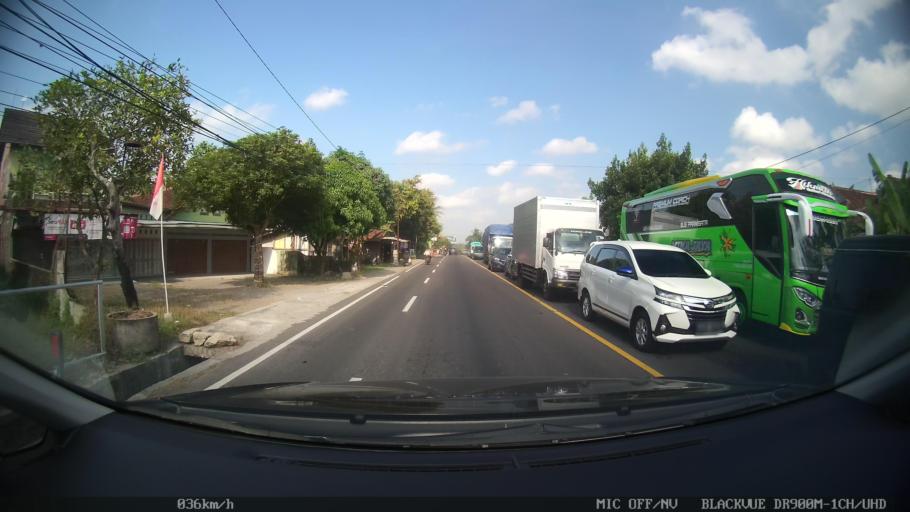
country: ID
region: Daerah Istimewa Yogyakarta
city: Godean
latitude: -7.8210
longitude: 110.2389
